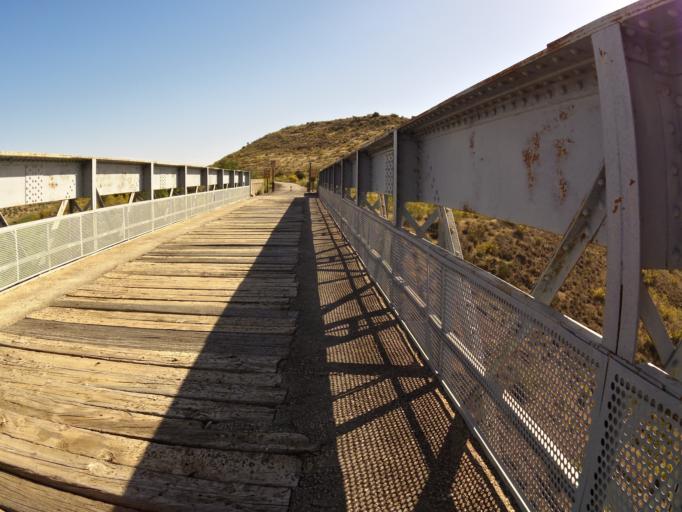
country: ES
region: Andalusia
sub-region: Province of Cordoba
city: Fuente-Tojar
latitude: 37.5880
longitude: -4.1691
